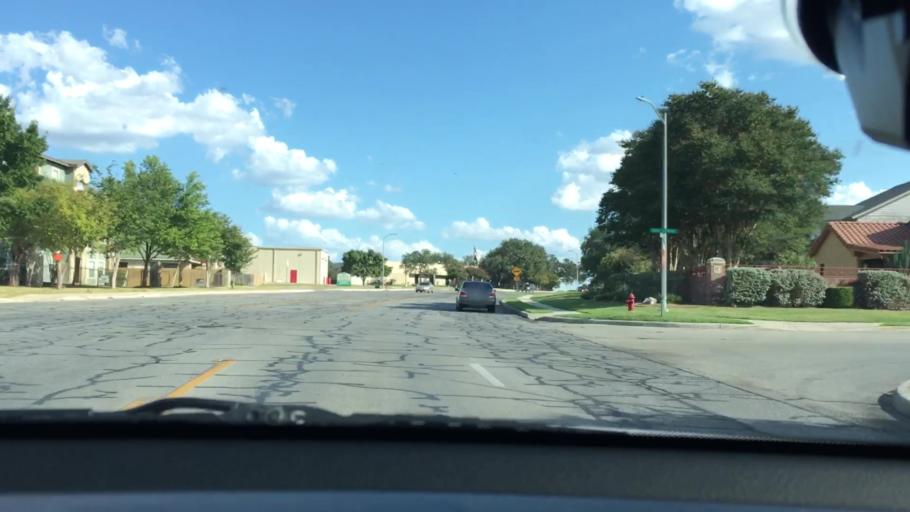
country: US
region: Texas
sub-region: Bexar County
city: Universal City
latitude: 29.5588
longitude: -98.3093
